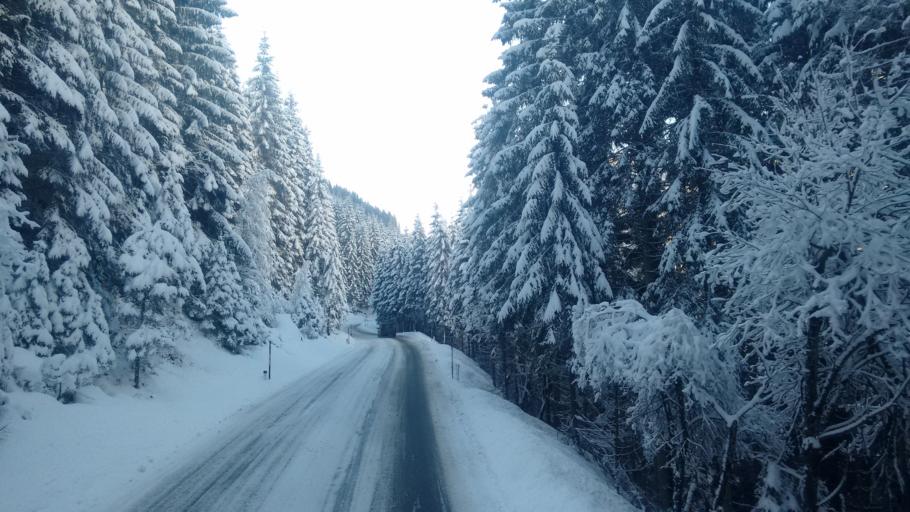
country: AT
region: Salzburg
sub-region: Politischer Bezirk Sankt Johann im Pongau
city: Untertauern
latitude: 47.3189
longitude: 13.4477
